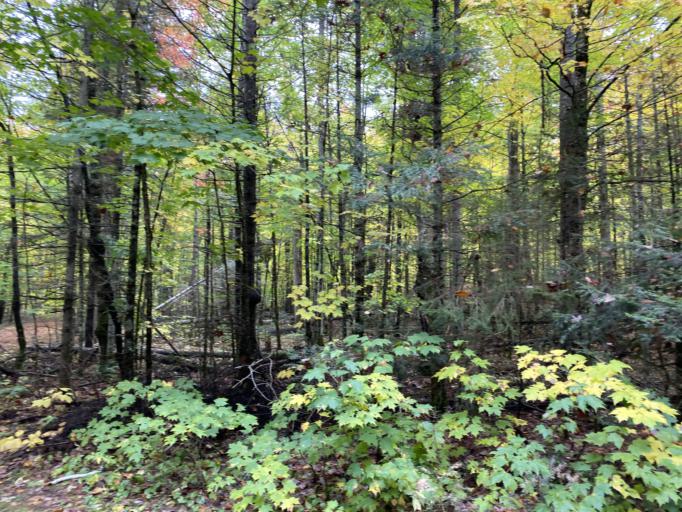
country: US
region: Michigan
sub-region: Marquette County
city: West Ishpeming
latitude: 46.5316
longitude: -87.9977
